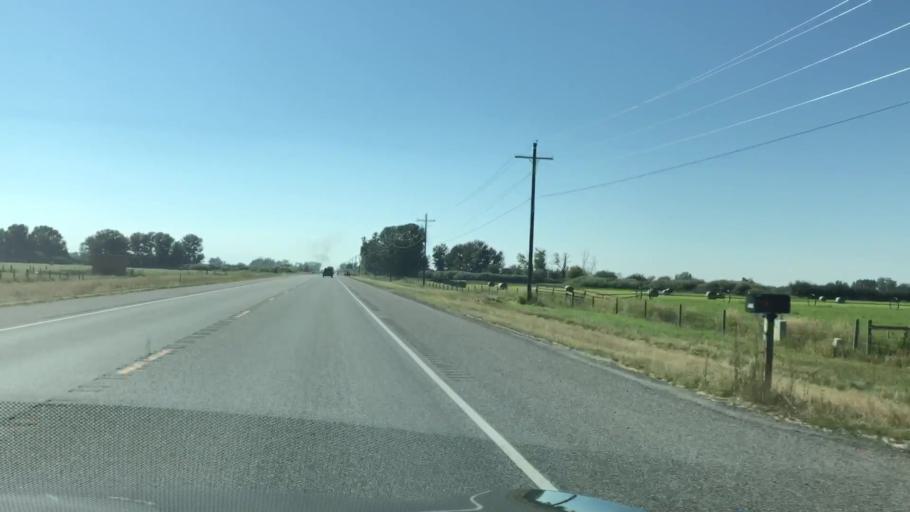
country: US
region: Montana
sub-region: Gallatin County
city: Belgrade
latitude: 45.7292
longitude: -111.1486
